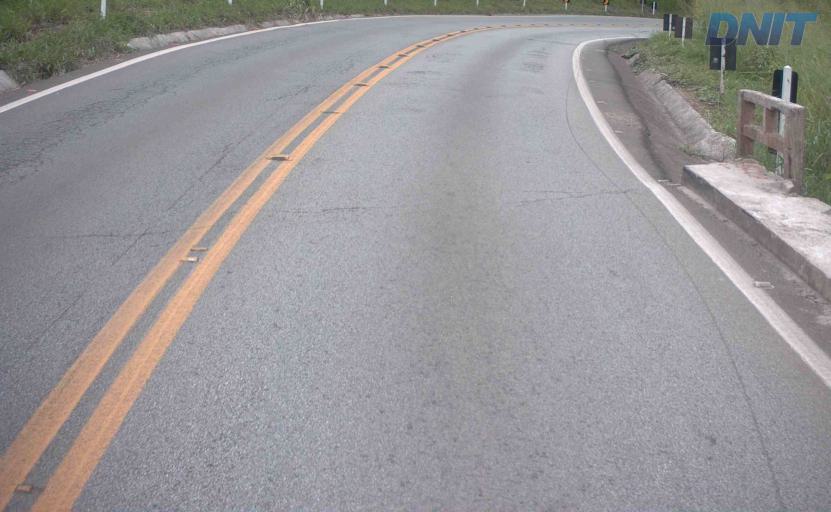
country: BR
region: Minas Gerais
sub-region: Nova Era
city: Nova Era
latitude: -19.7724
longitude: -43.0466
